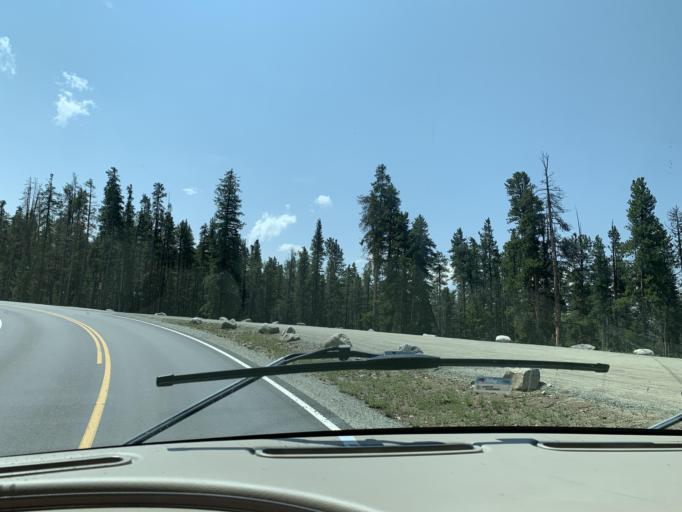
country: US
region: Colorado
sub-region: Chaffee County
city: Buena Vista
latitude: 38.8459
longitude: -106.4888
